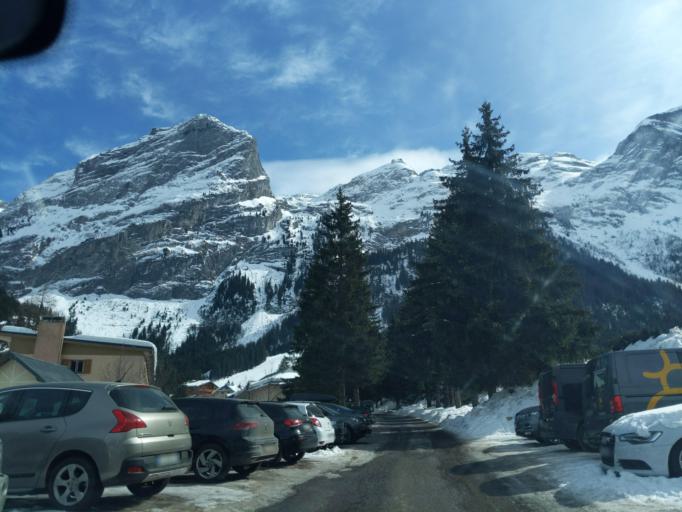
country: FR
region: Rhone-Alpes
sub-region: Departement de la Savoie
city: Courchevel
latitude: 45.3814
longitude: 6.7196
